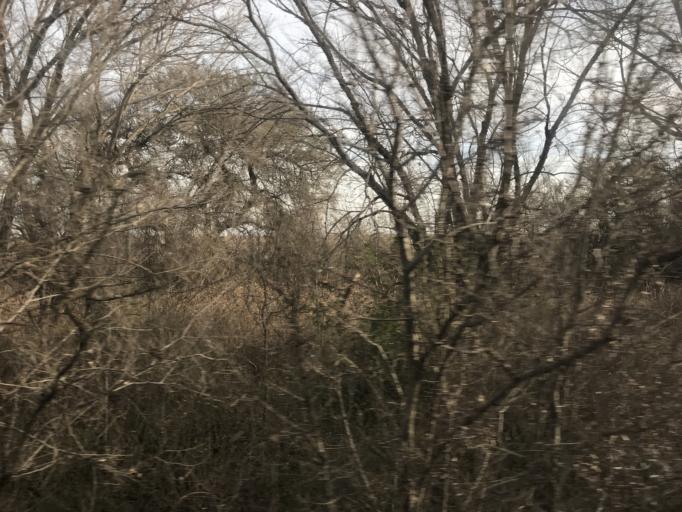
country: AR
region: Cordoba
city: Pilar
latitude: -31.7024
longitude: -63.8681
